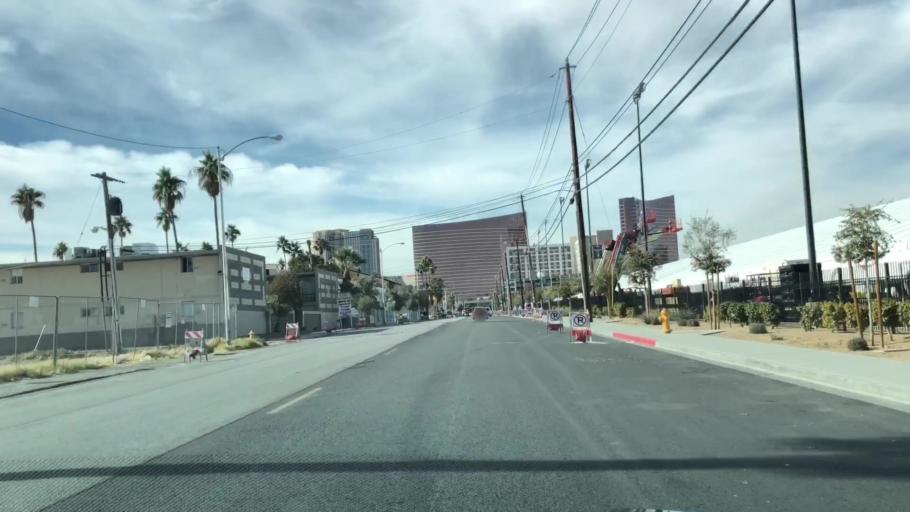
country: US
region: Nevada
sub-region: Clark County
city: Winchester
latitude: 36.1269
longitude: -115.1478
